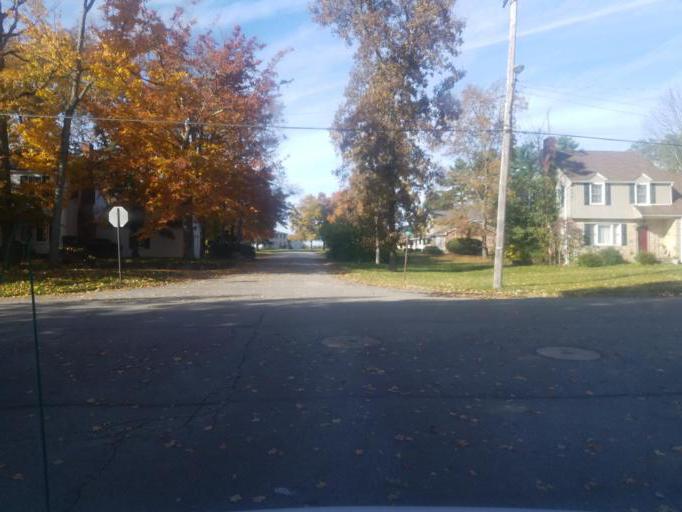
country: US
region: Ohio
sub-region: Richland County
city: Mansfield
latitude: 40.7313
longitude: -82.5414
